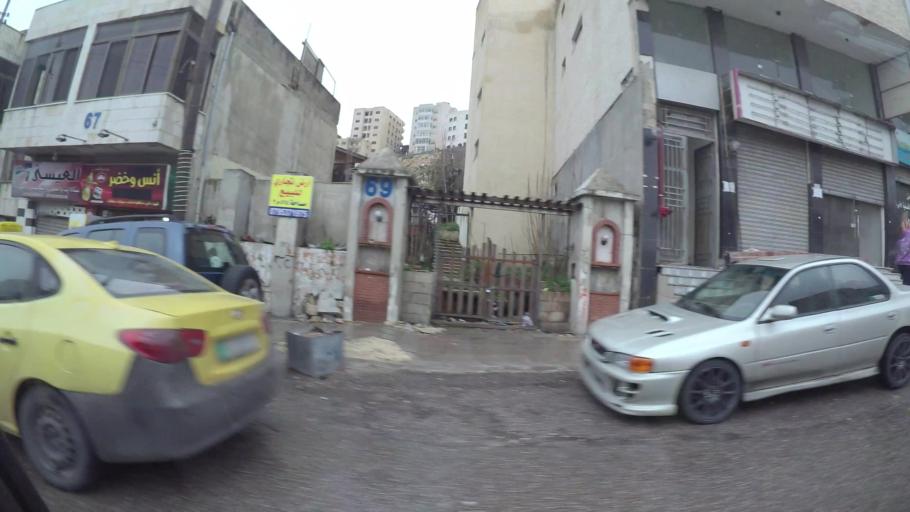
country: JO
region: Amman
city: Al Jubayhah
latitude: 32.0255
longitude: 35.8380
